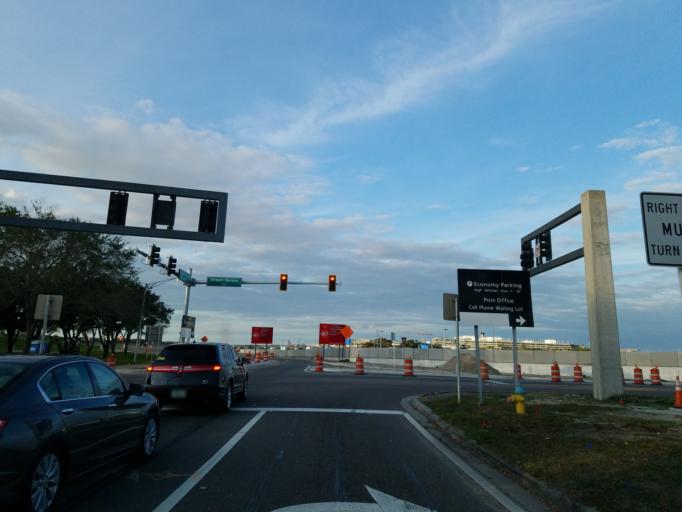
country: US
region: Florida
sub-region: Hillsborough County
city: Town 'n' Country
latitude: 27.9685
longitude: -82.5386
